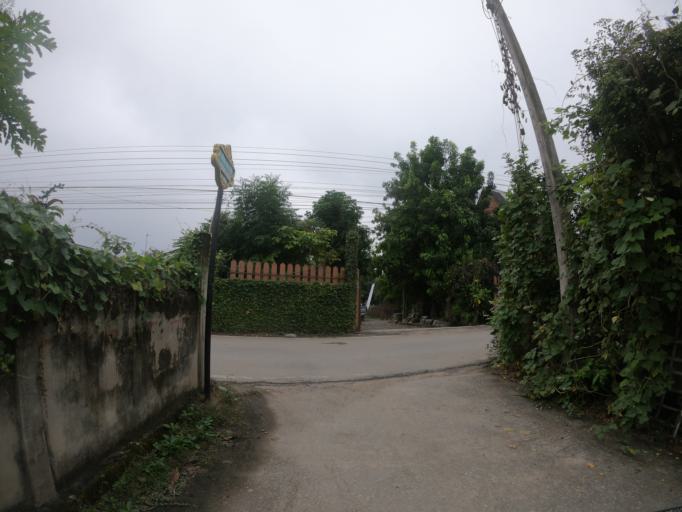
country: TH
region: Chiang Mai
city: Hang Dong
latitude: 18.7412
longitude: 98.9480
